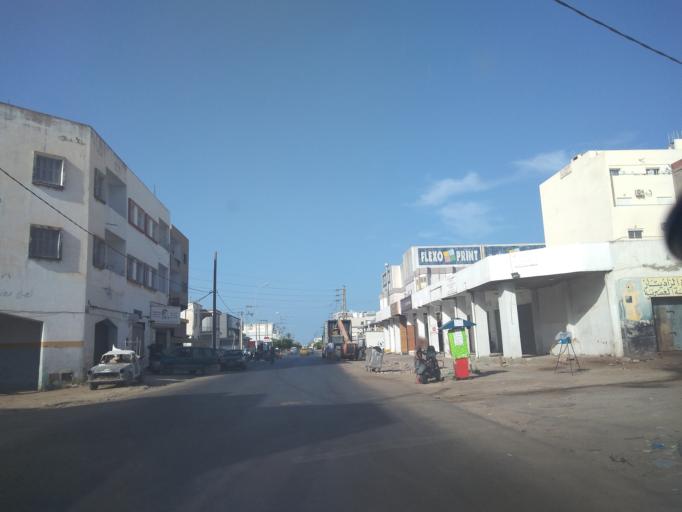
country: TN
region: Safaqis
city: Sfax
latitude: 34.7451
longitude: 10.7685
